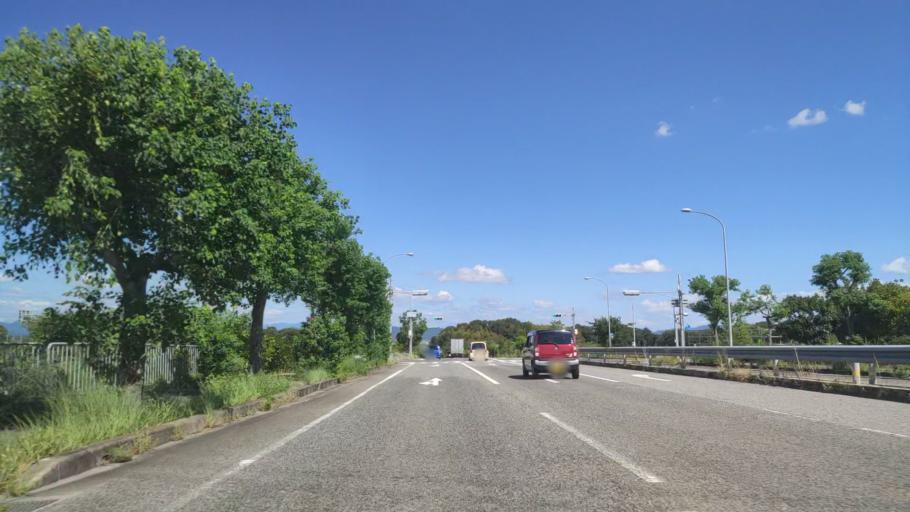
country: JP
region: Hyogo
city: Ono
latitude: 34.8717
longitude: 134.9521
